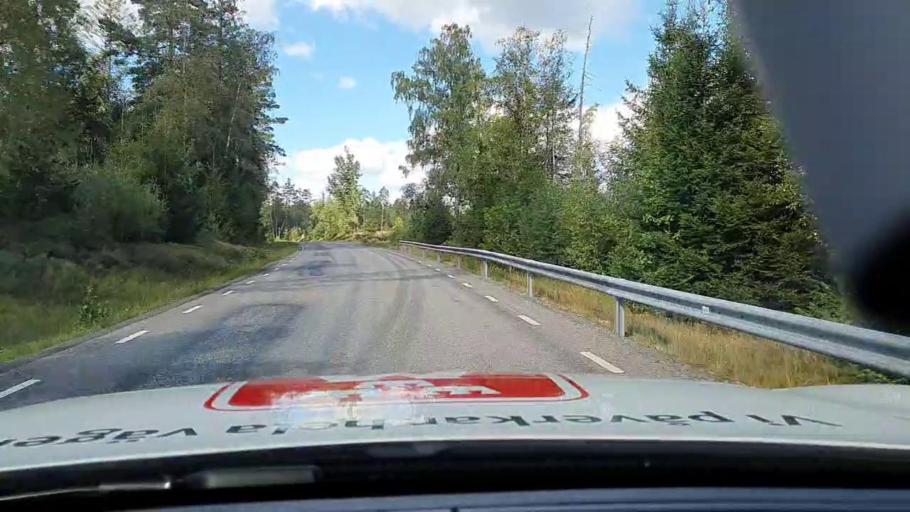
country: SE
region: Vaestra Goetaland
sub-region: Marks Kommun
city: Fritsla
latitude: 57.3671
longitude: 12.8648
